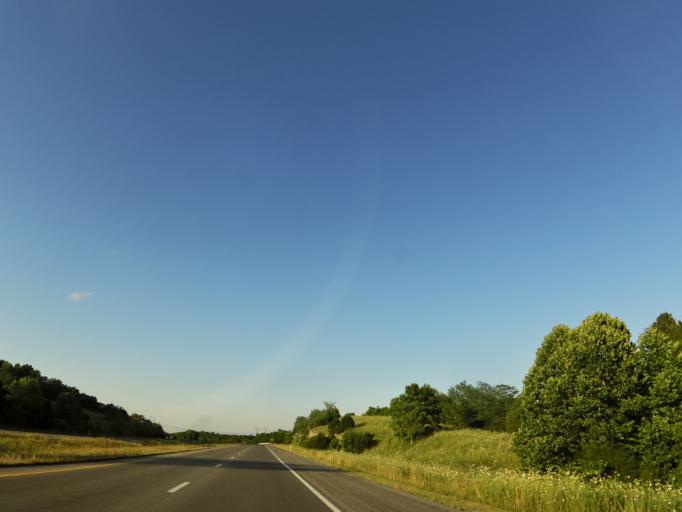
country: US
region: Tennessee
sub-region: Wilson County
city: Lebanon
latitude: 36.1446
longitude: -86.3721
